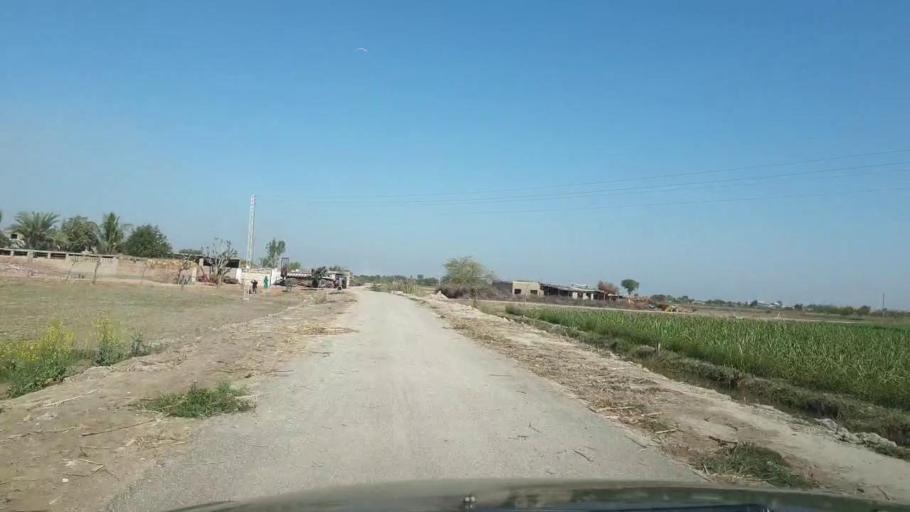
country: PK
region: Sindh
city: Mirpur Khas
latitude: 25.5658
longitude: 69.0565
